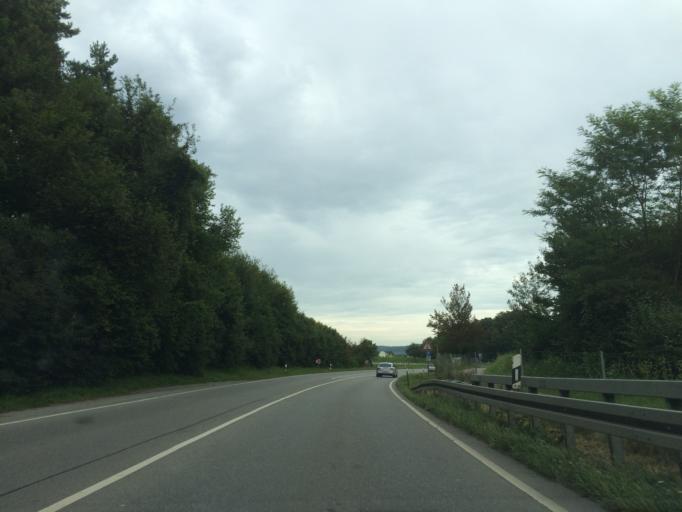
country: DE
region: Baden-Wuerttemberg
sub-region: Tuebingen Region
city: Ravensburg
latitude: 47.7737
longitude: 9.5666
